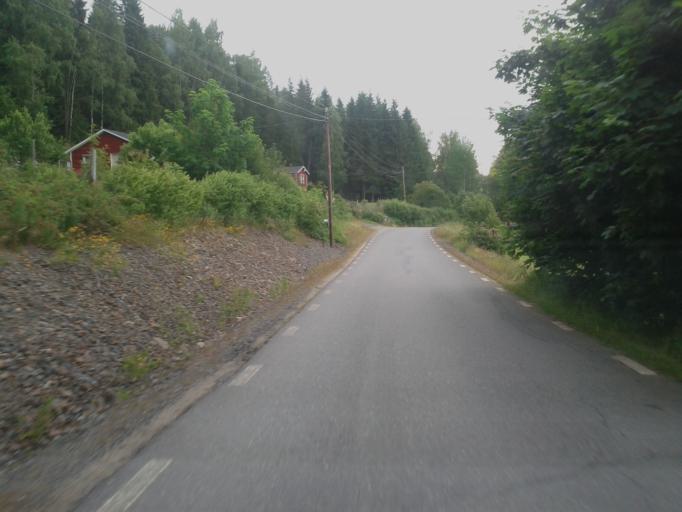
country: SE
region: Vaesternorrland
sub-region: Kramfors Kommun
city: Nordingra
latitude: 63.0621
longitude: 18.3922
